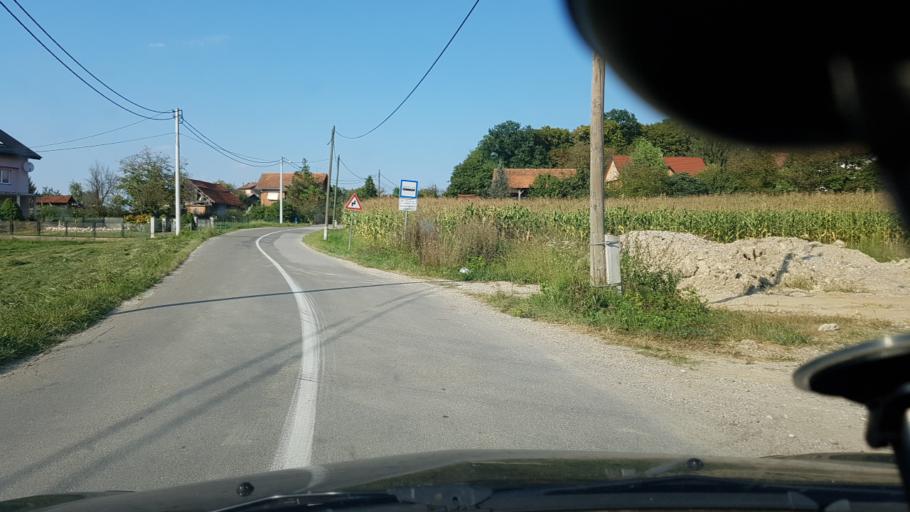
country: HR
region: Zagrebacka
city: Bregana
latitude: 45.9102
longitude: 15.6940
